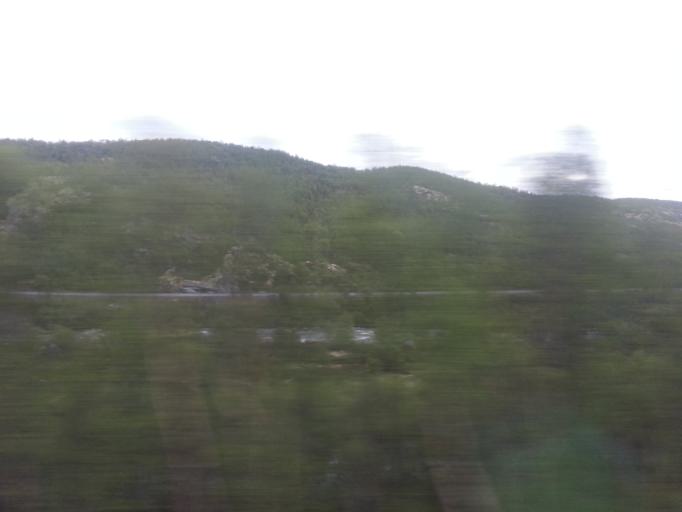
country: NO
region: Sor-Trondelag
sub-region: Oppdal
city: Oppdal
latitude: 62.2941
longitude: 9.5914
